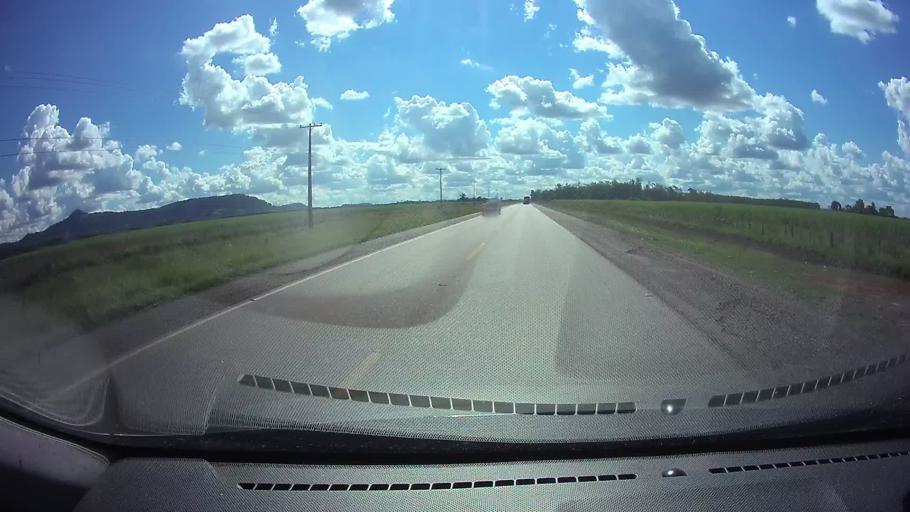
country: PY
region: Paraguari
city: La Colmena
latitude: -25.7571
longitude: -56.7610
